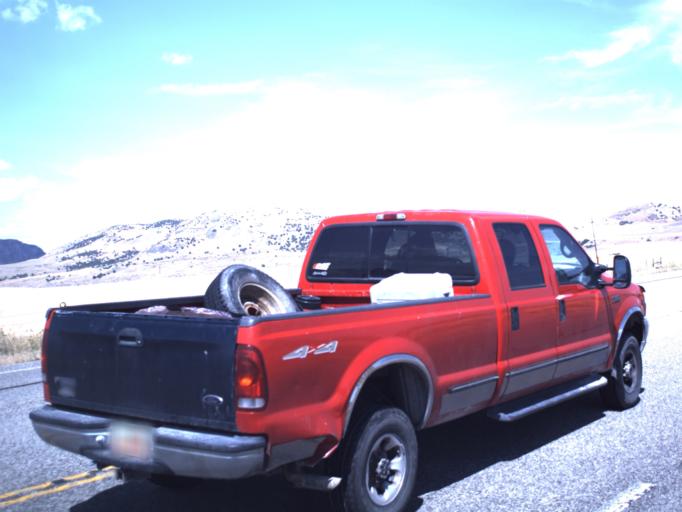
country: US
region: Utah
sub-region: Box Elder County
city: Garland
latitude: 41.7940
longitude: -112.0590
